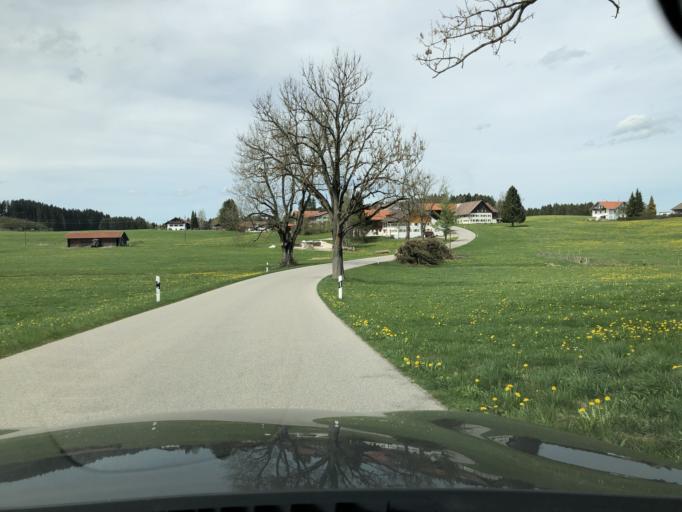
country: DE
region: Bavaria
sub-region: Swabia
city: Wald
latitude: 47.7049
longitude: 10.5572
